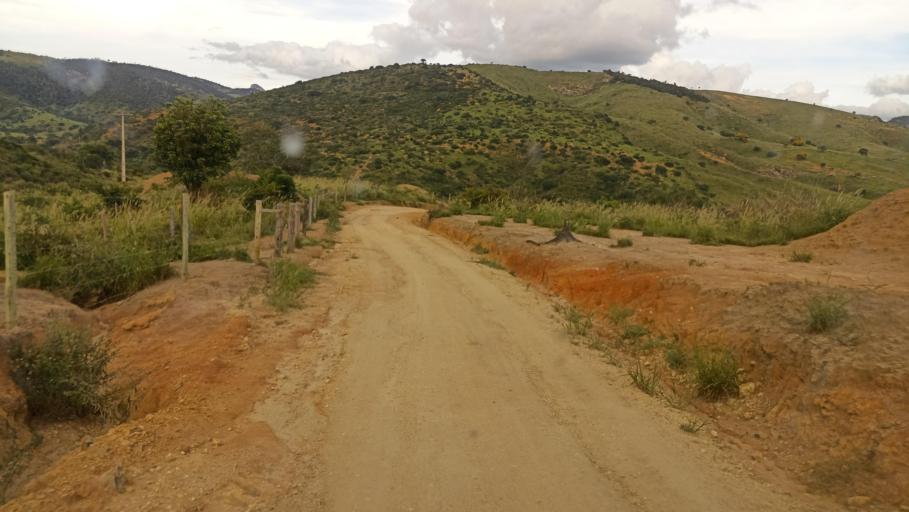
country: BR
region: Minas Gerais
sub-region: Almenara
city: Almenara
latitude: -16.5383
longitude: -40.4443
